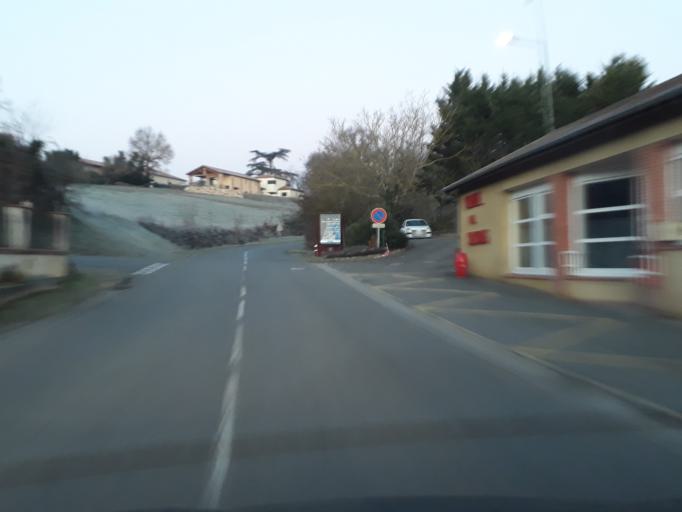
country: FR
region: Midi-Pyrenees
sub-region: Departement du Gers
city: Samatan
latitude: 43.4920
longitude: 0.9283
